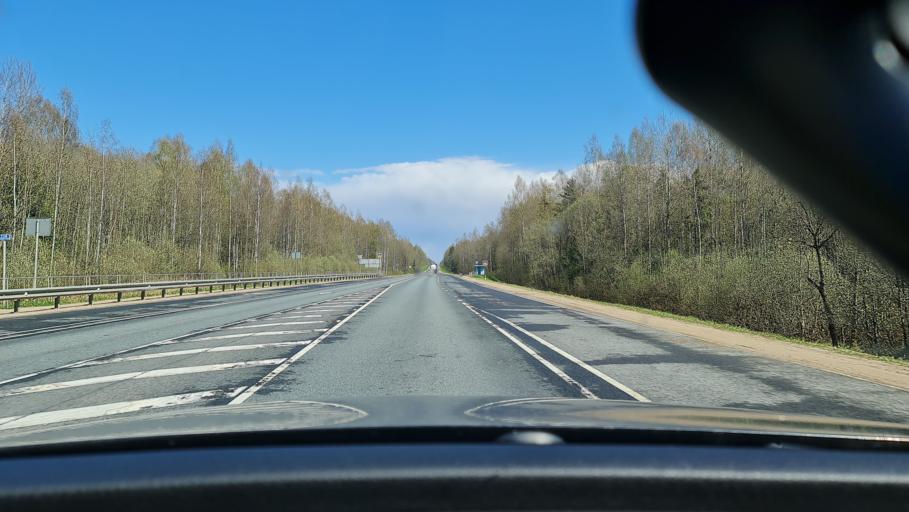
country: RU
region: Tverskaya
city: Rzhev
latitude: 56.2112
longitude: 34.1123
